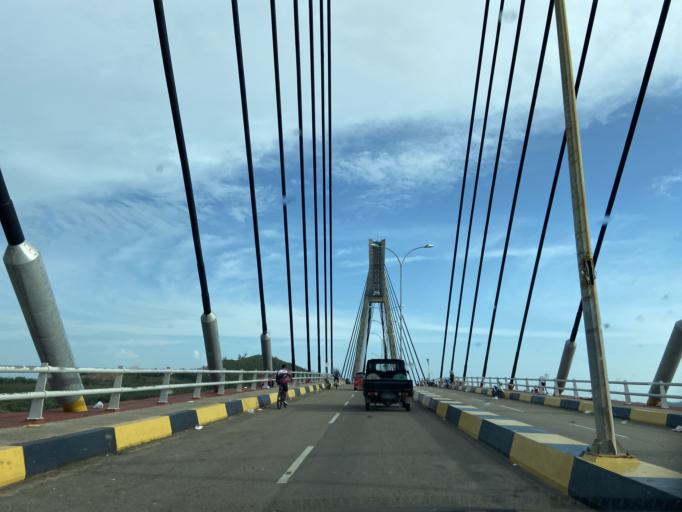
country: SG
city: Singapore
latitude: 0.9805
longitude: 104.0419
